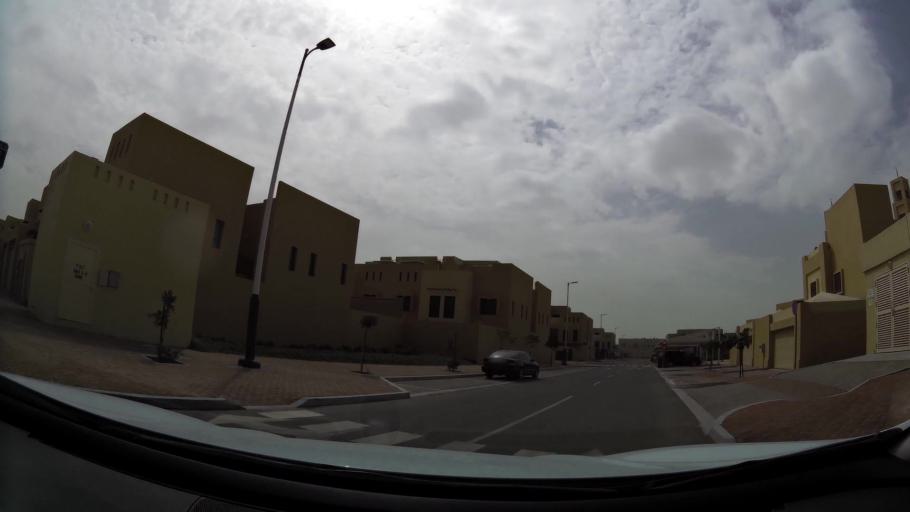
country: AE
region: Abu Dhabi
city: Abu Dhabi
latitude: 24.4000
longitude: 54.4894
